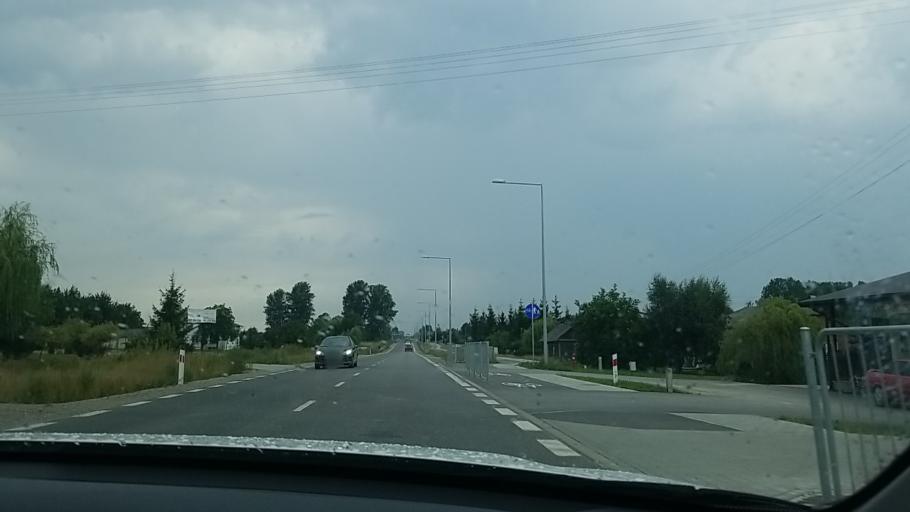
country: PL
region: Lublin Voivodeship
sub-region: Powiat lubelski
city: Jablonna
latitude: 51.0451
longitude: 22.6369
